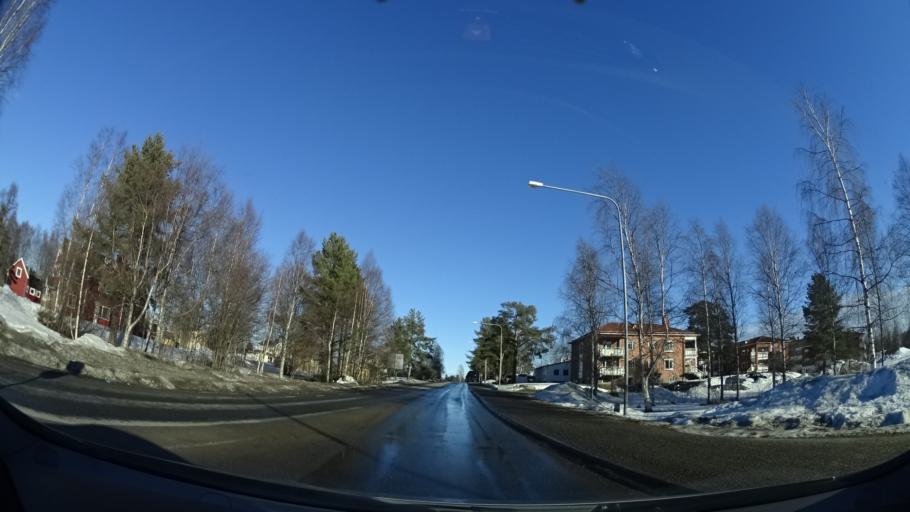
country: SE
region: Vaesterbotten
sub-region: Skelleftea Kommun
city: Byske
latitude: 64.9521
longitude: 21.1935
